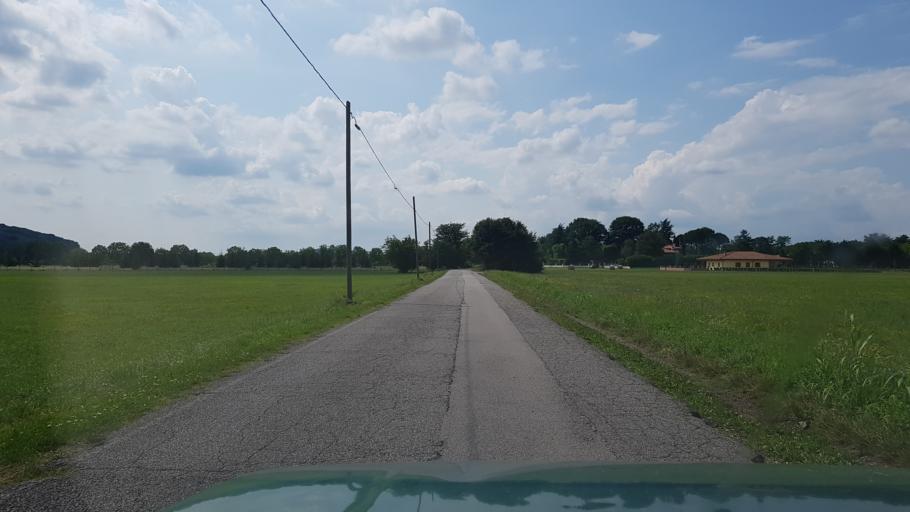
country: IT
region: Friuli Venezia Giulia
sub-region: Provincia di Gorizia
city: Savogna d'Isonzo
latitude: 45.8998
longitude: 13.5827
